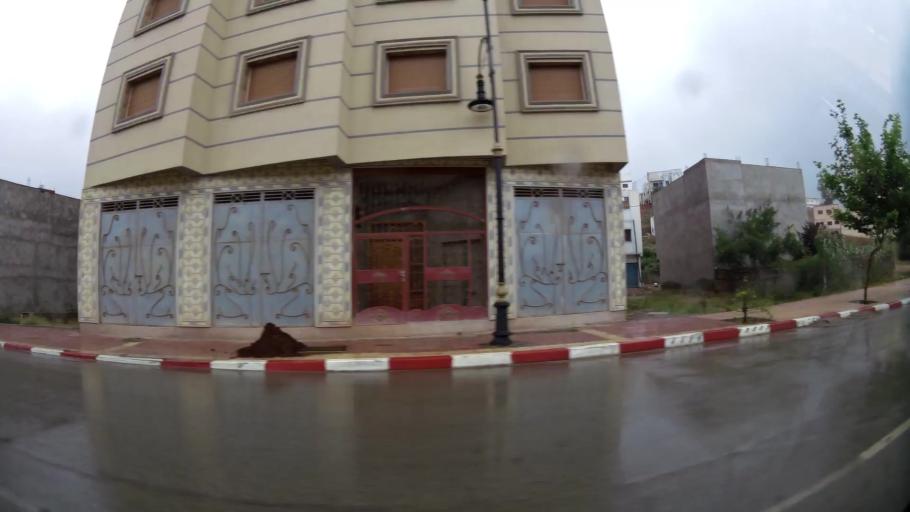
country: MA
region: Taza-Al Hoceima-Taounate
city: Imzourene
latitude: 35.1555
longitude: -3.8494
